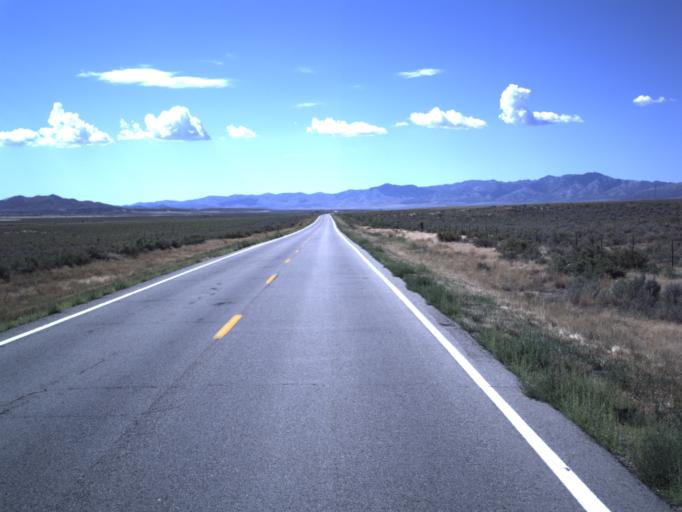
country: US
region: Utah
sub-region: Tooele County
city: Tooele
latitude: 40.2257
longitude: -112.4043
